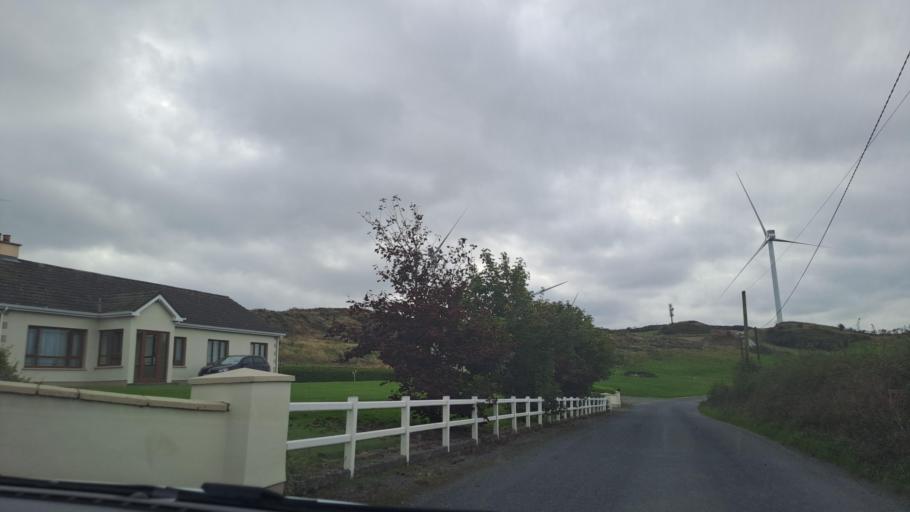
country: IE
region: Ulster
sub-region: An Cabhan
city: Kingscourt
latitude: 53.9577
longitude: -6.8802
